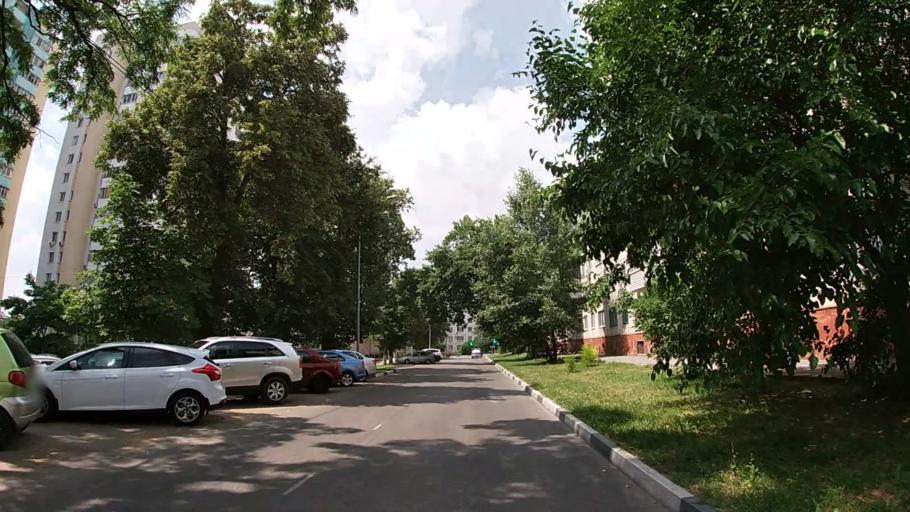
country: RU
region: Belgorod
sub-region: Belgorodskiy Rayon
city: Belgorod
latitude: 50.6044
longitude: 36.5973
